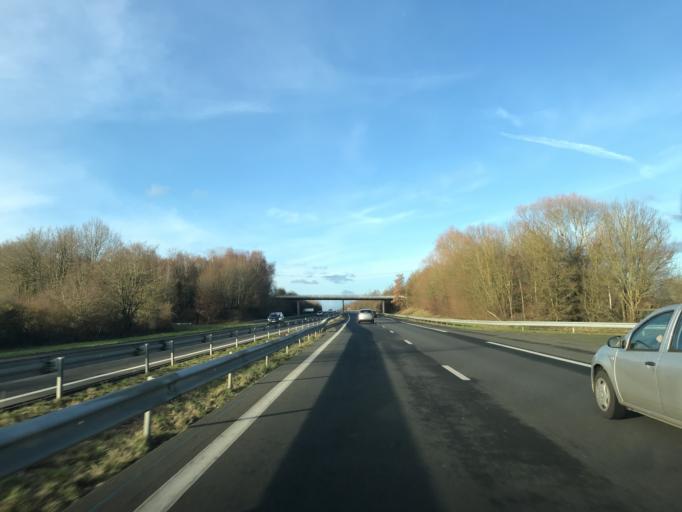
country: FR
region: Pays de la Loire
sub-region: Departement de Maine-et-Loire
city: Durtal
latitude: 47.7019
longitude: -0.2489
